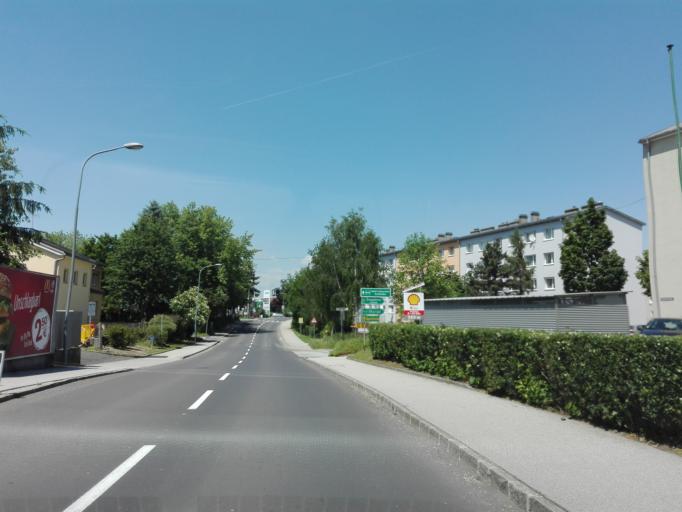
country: AT
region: Upper Austria
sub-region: Politischer Bezirk Linz-Land
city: Traun
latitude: 48.2017
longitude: 14.2506
